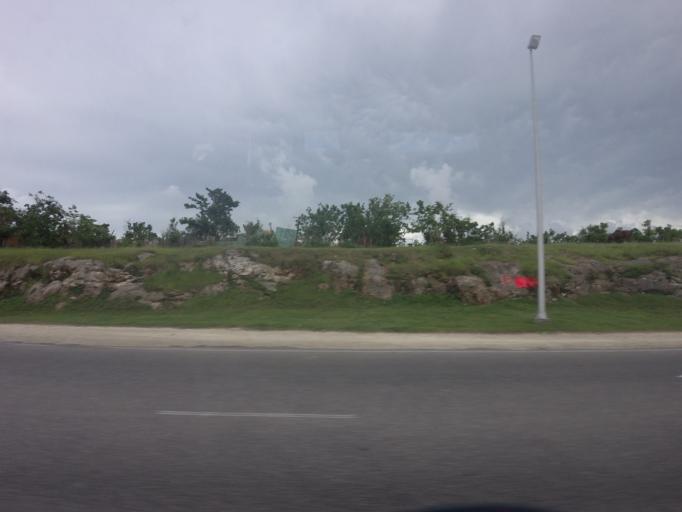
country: CU
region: Matanzas
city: Varadero
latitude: 23.1095
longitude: -81.3661
